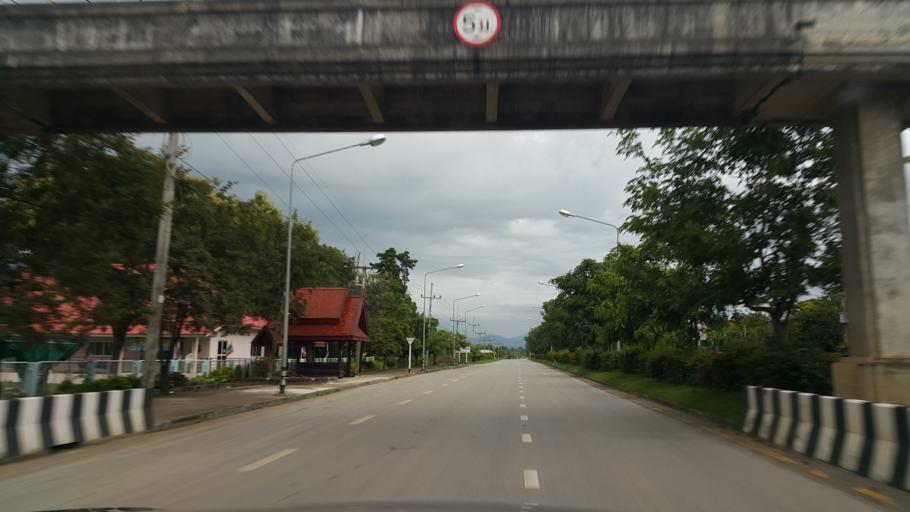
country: TH
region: Phayao
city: Dok Kham Tai
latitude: 19.1734
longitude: 100.0075
